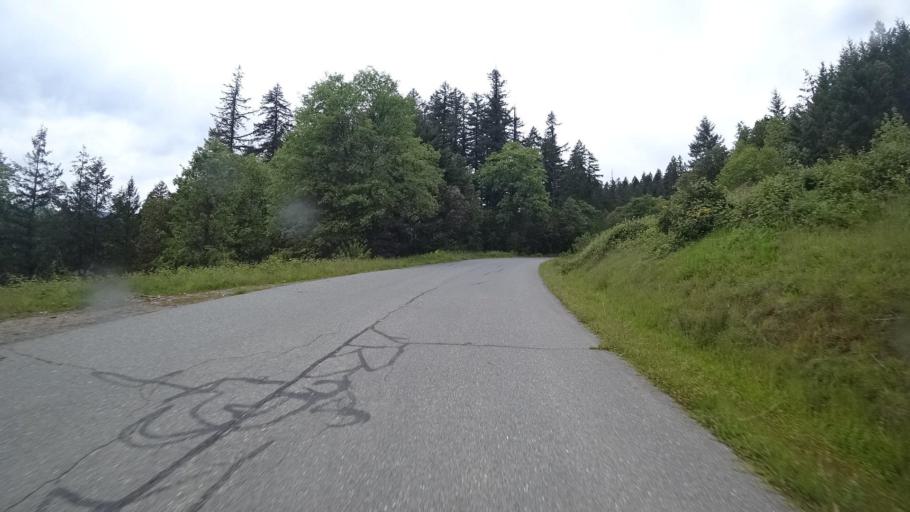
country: US
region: California
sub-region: Humboldt County
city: Willow Creek
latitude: 41.1208
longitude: -123.7418
